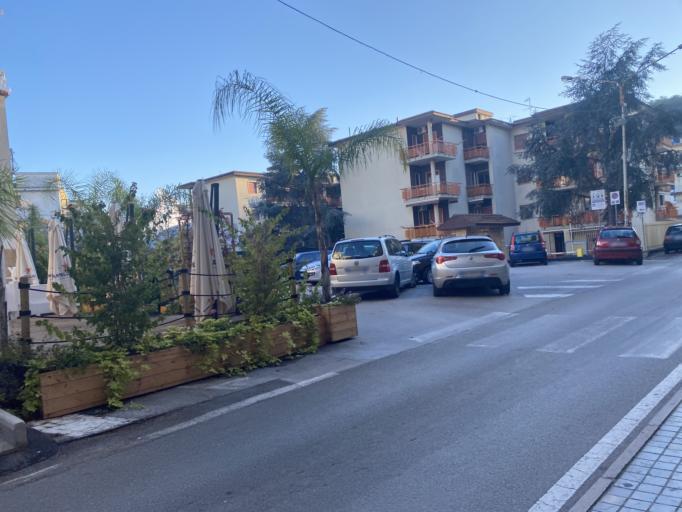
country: IT
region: Campania
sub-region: Provincia di Salerno
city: Agropoli
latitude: 40.3500
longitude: 14.9898
